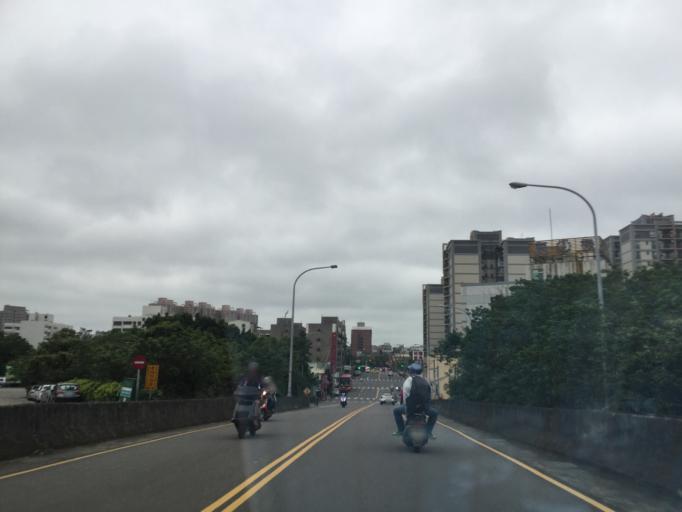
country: TW
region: Taiwan
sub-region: Hsinchu
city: Hsinchu
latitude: 24.7965
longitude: 121.0068
